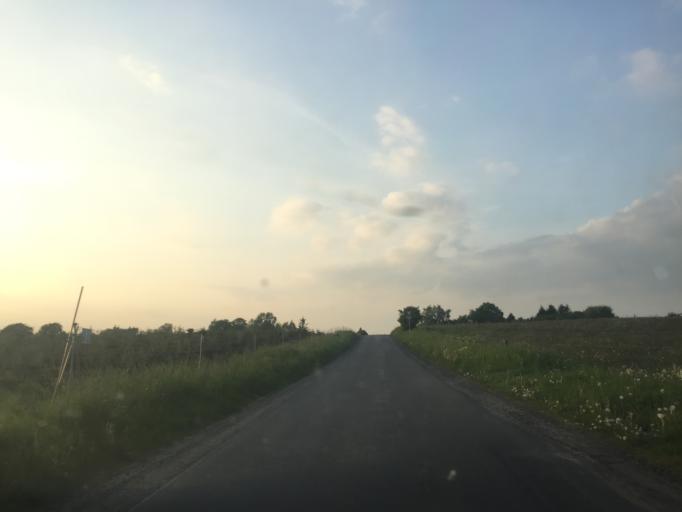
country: DK
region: South Denmark
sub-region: Odense Kommune
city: Bellinge
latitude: 55.3785
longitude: 10.3103
